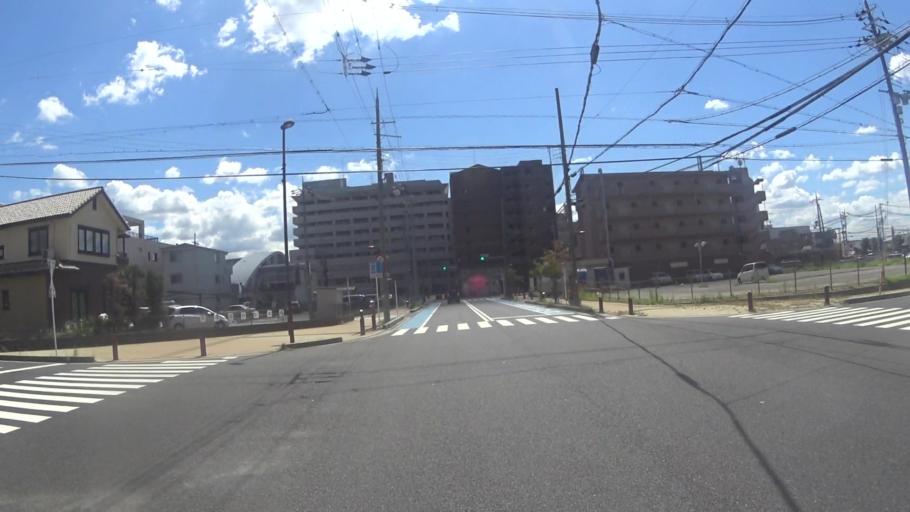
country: JP
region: Nara
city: Nara-shi
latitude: 34.7374
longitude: 135.8240
